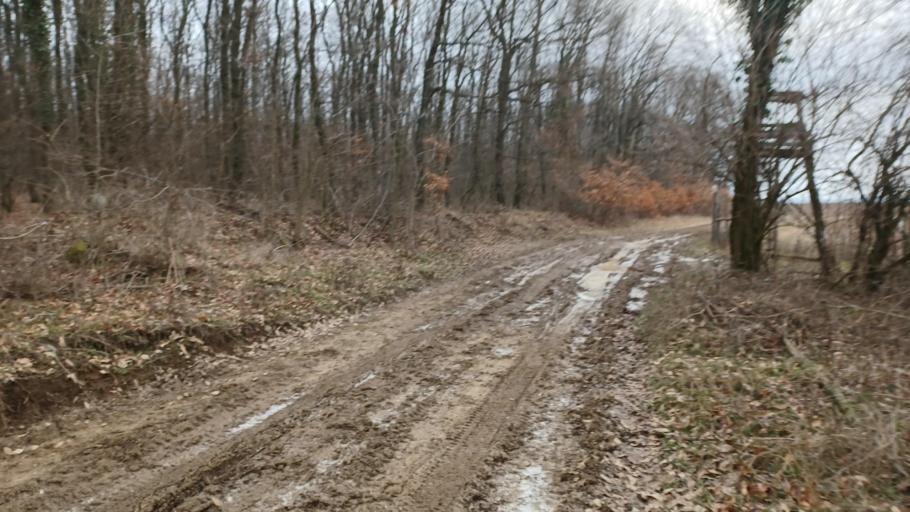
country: HU
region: Tolna
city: Szentgalpuszta
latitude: 46.2964
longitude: 18.6277
